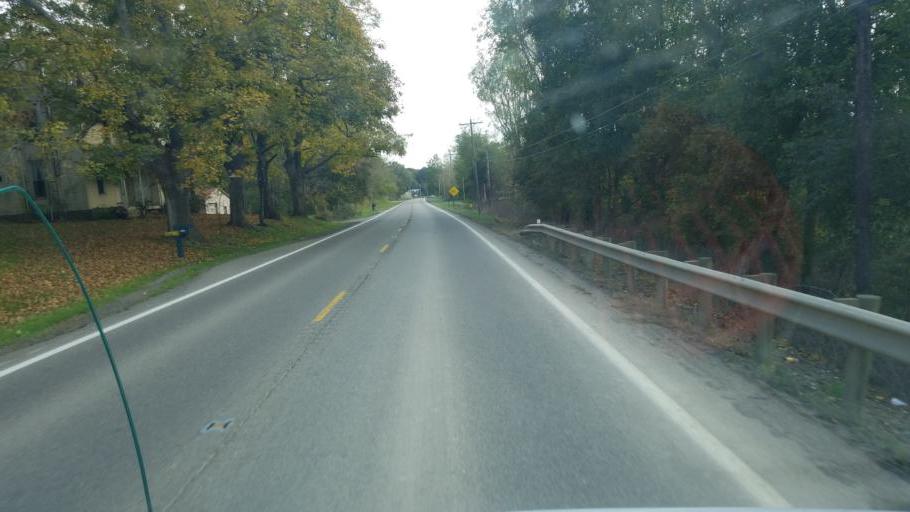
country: US
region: Ohio
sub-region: Wayne County
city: Shreve
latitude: 40.6566
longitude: -81.9413
